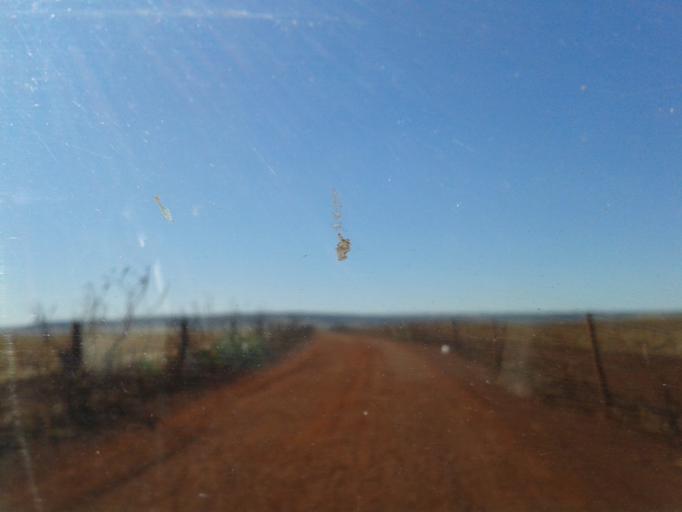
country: BR
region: Minas Gerais
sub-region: Centralina
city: Centralina
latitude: -18.5852
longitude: -49.1396
